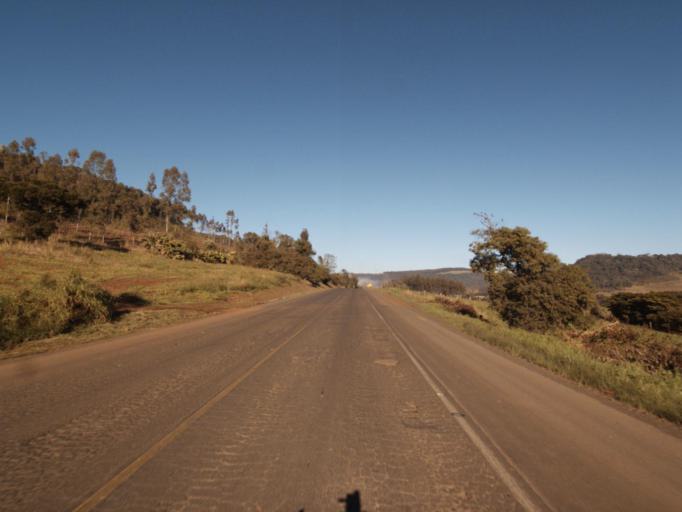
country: BR
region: Rio Grande do Sul
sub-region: Frederico Westphalen
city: Frederico Westphalen
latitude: -26.9613
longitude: -53.2070
